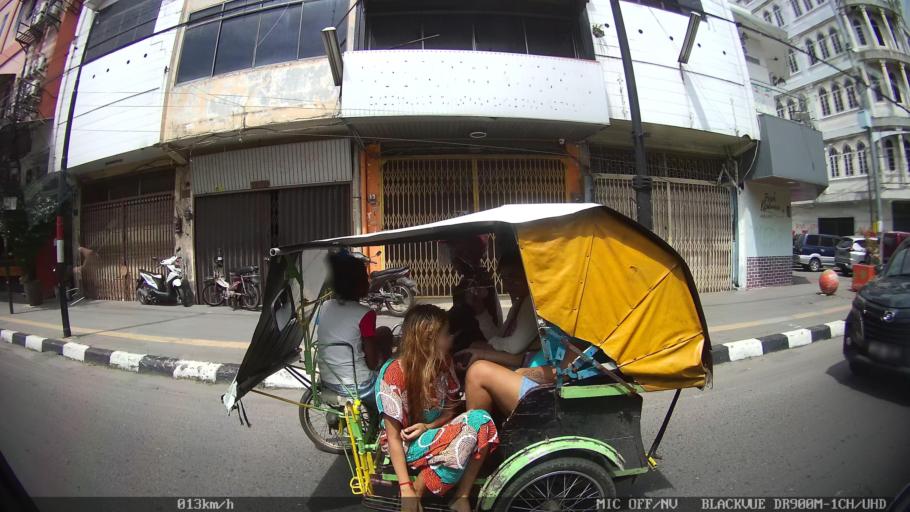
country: ID
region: North Sumatra
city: Medan
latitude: 3.5856
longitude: 98.6801
